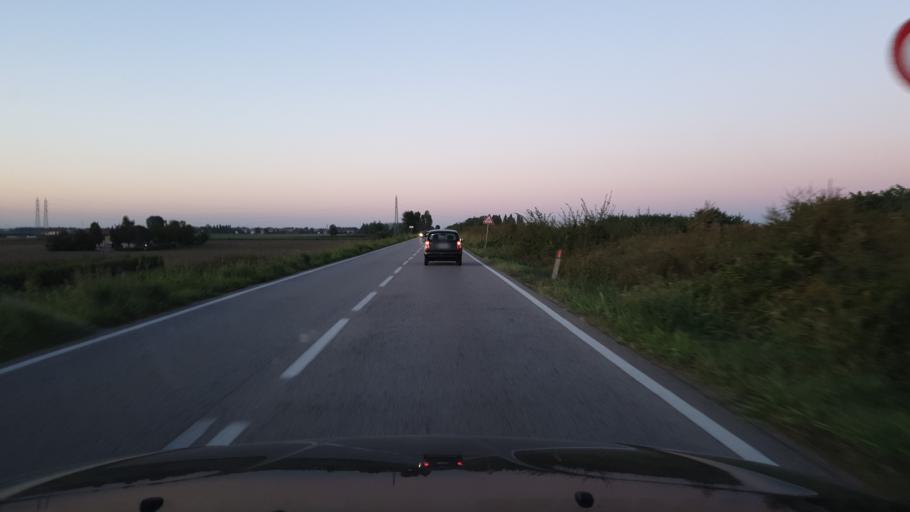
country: IT
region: Emilia-Romagna
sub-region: Provincia di Bologna
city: Minerbio
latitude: 44.6415
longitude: 11.4744
